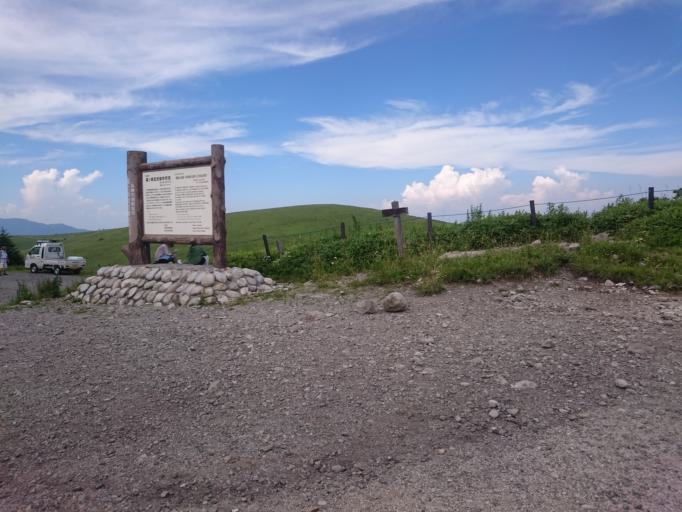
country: JP
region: Nagano
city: Suwa
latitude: 36.1045
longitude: 138.1883
